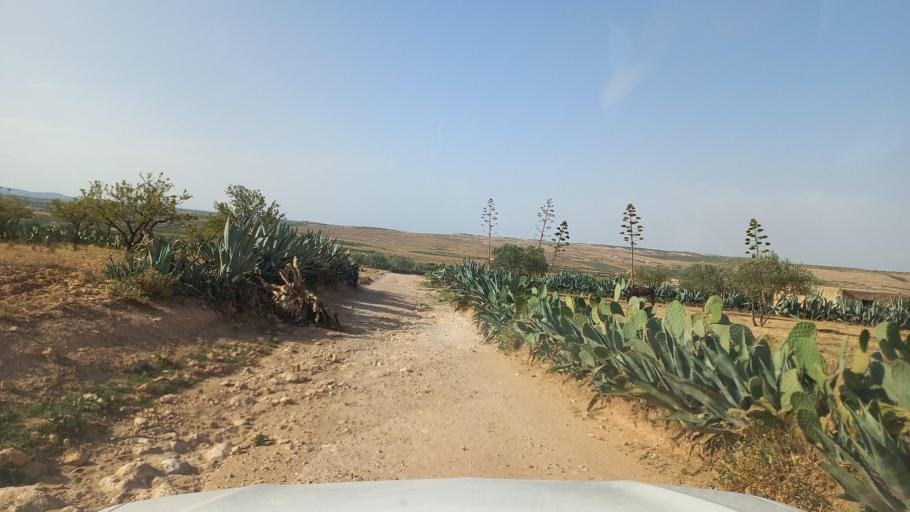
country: TN
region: Al Qasrayn
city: Kasserine
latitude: 35.3356
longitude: 8.8453
